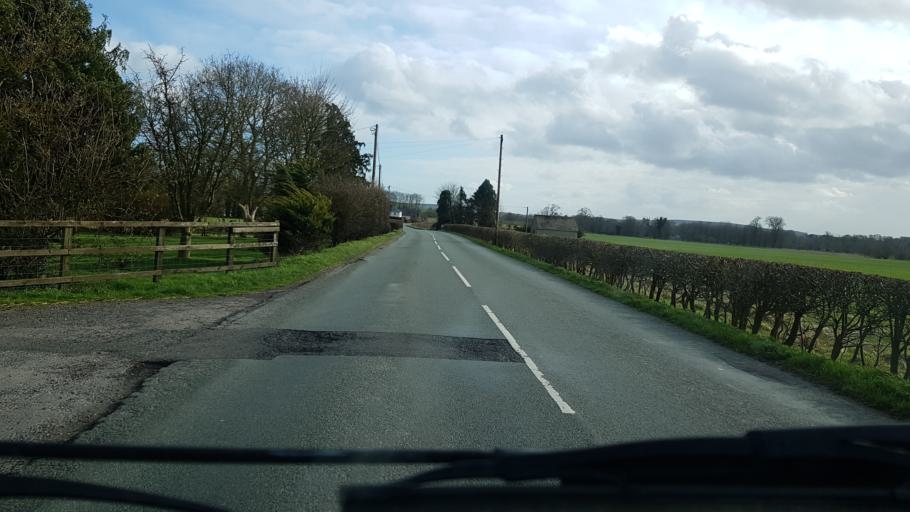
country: GB
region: England
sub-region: Wiltshire
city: Avebury
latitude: 51.4360
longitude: -1.8550
